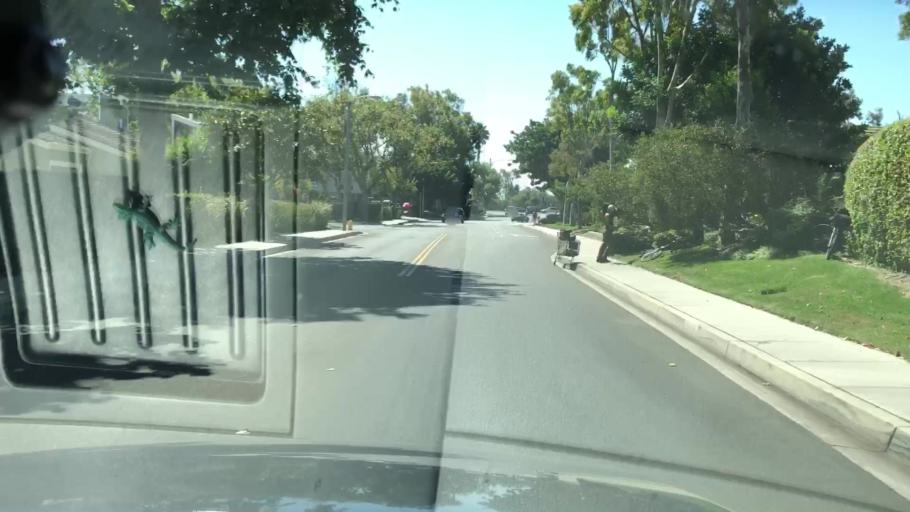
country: US
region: California
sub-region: Ventura County
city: Channel Islands Beach
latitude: 34.1776
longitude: -119.2126
